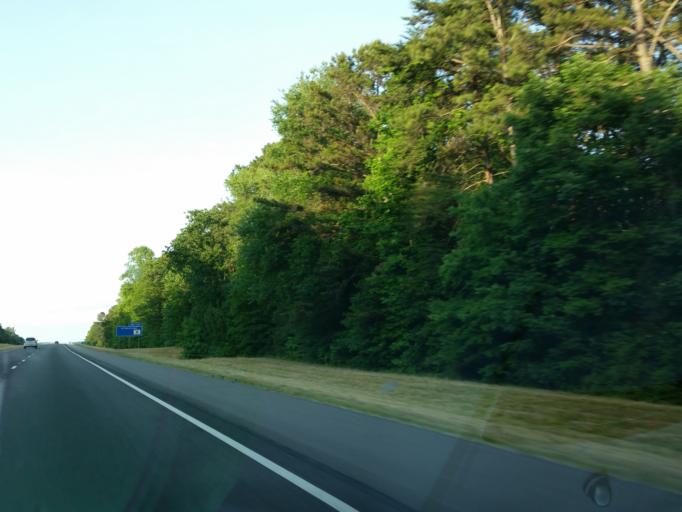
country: US
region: Alabama
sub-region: DeKalb County
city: Henagar
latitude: 34.5813
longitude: -85.6526
